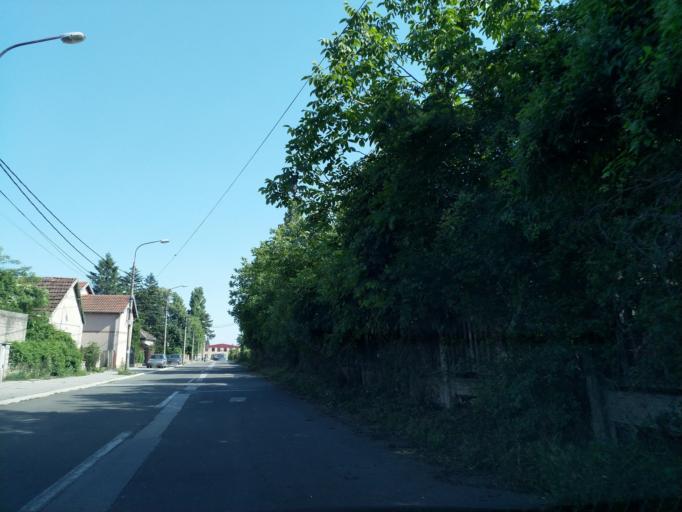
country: RS
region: Central Serbia
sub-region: Pomoravski Okrug
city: Paracin
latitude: 43.8641
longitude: 21.4001
